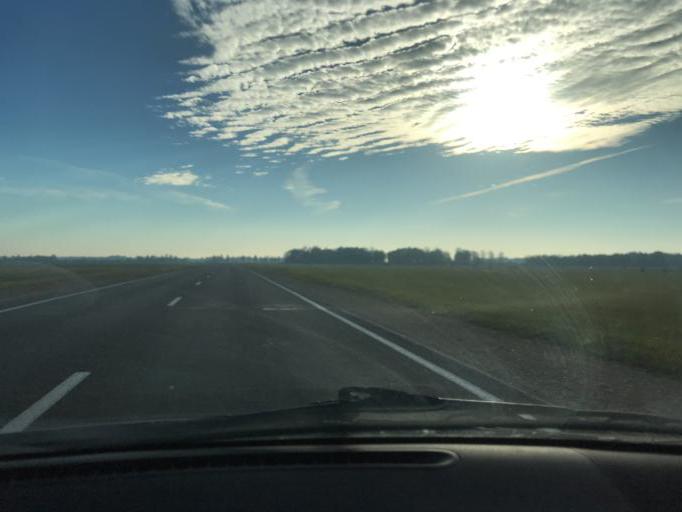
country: BY
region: Brest
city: Drahichyn
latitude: 52.2108
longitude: 25.2031
